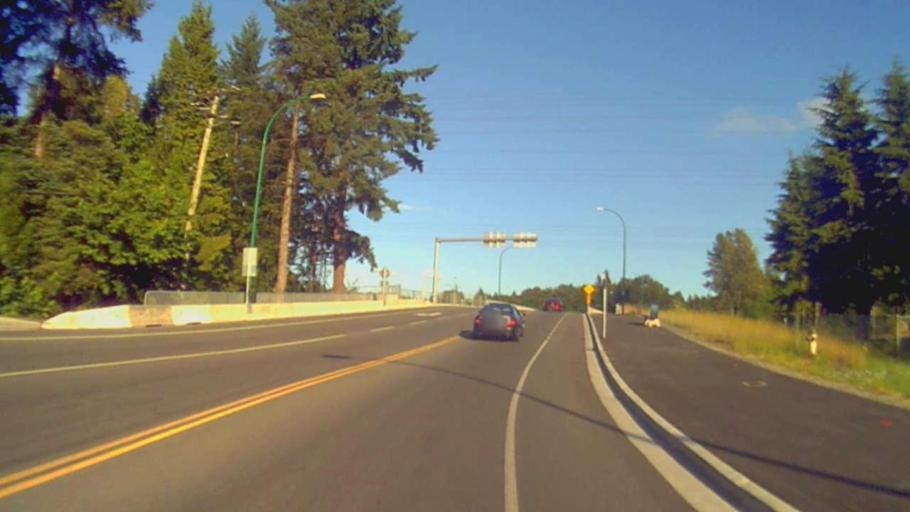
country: CA
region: British Columbia
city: New Westminster
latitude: 49.2453
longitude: -122.9109
